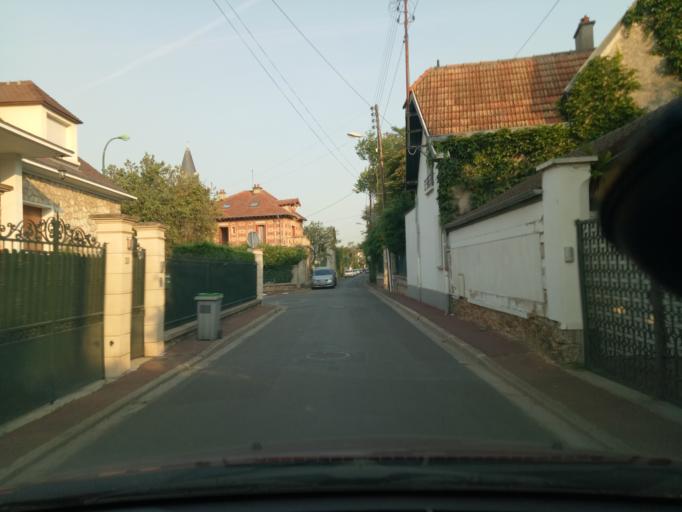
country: FR
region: Ile-de-France
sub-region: Departement des Yvelines
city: Croissy-sur-Seine
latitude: 48.8827
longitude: 2.1482
